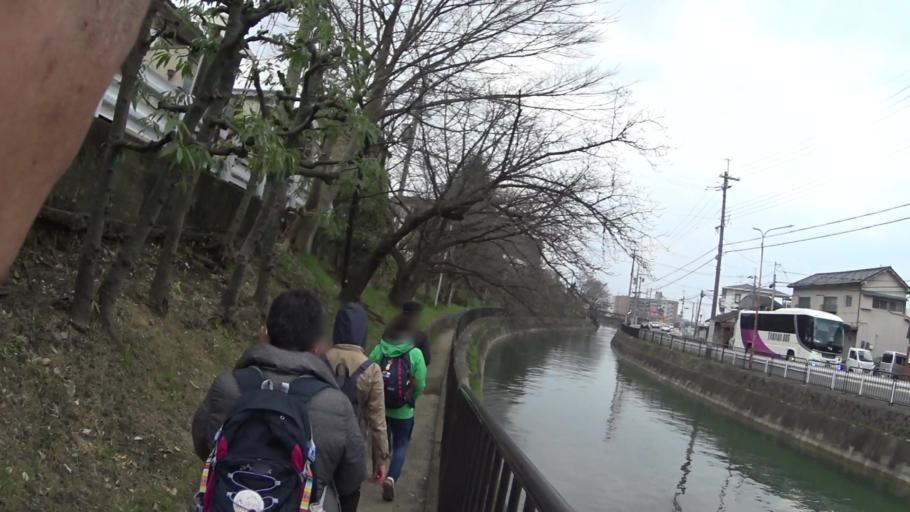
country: JP
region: Kyoto
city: Kyoto
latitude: 34.9776
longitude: 135.7717
